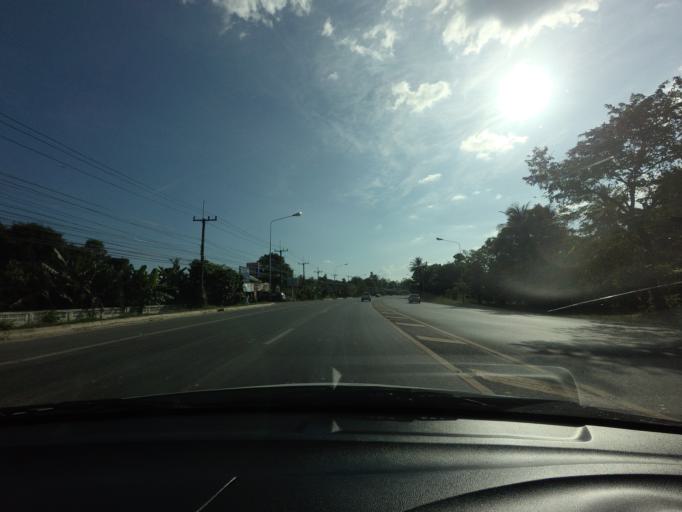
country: TH
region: Nakhon Nayok
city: Nakhon Nayok
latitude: 14.2681
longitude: 101.2726
